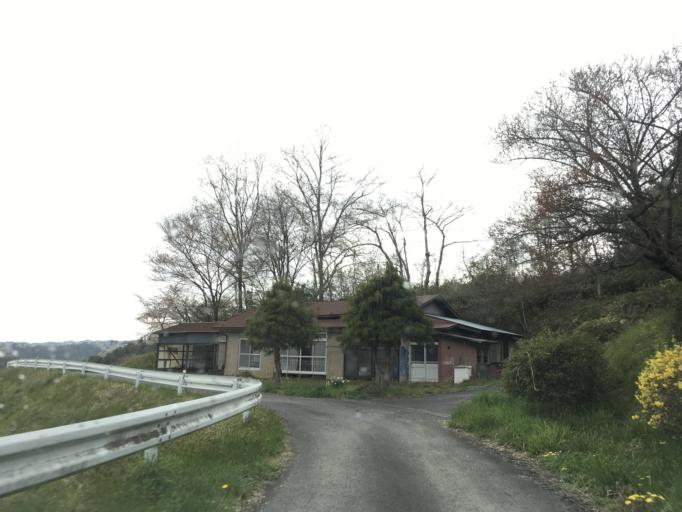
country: JP
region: Iwate
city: Ichinoseki
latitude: 38.8528
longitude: 141.3273
